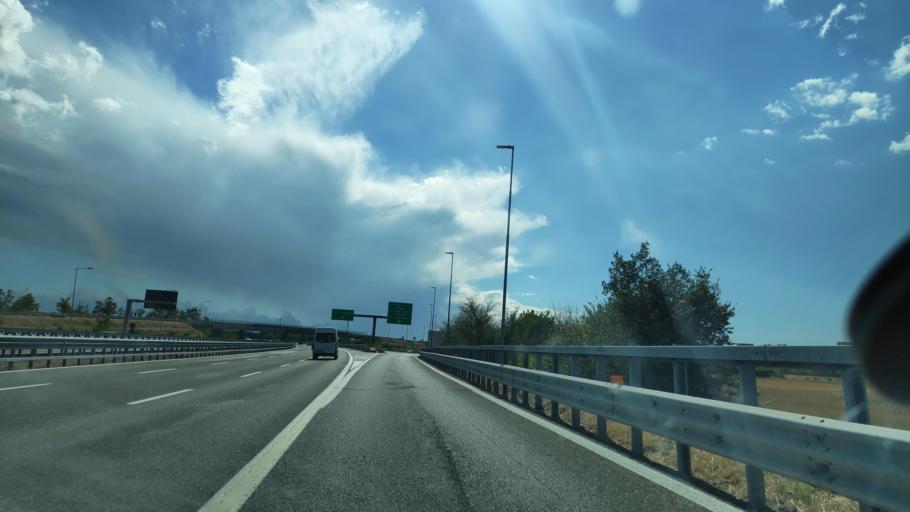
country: IT
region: Piedmont
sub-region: Provincia di Alessandria
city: Tortona
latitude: 44.9237
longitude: 8.8459
